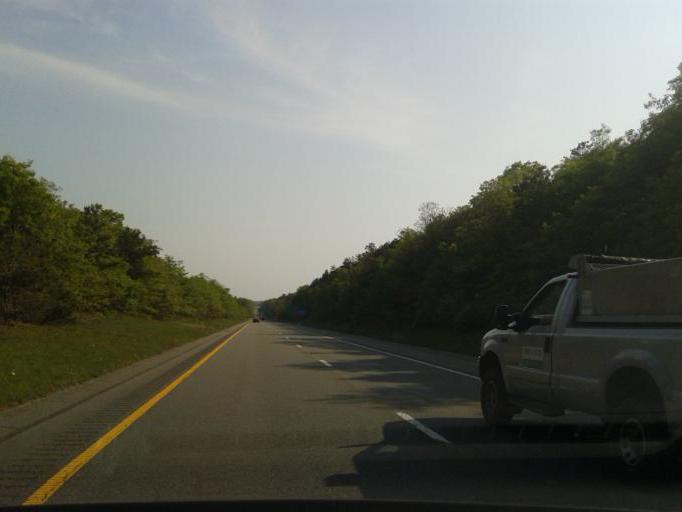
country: US
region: Massachusetts
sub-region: Barnstable County
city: North Falmouth
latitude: 41.6346
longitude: -70.6100
